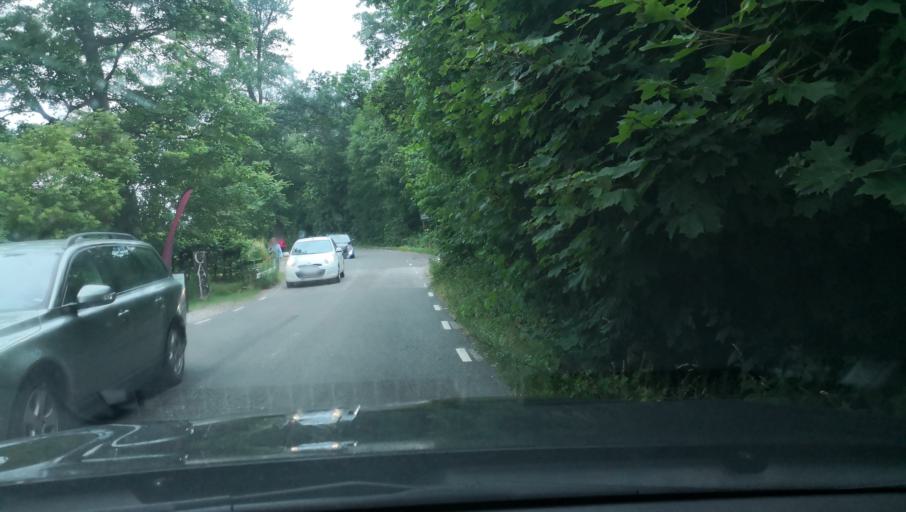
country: SE
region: Skane
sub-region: Simrishamns Kommun
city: Kivik
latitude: 55.6824
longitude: 14.2357
